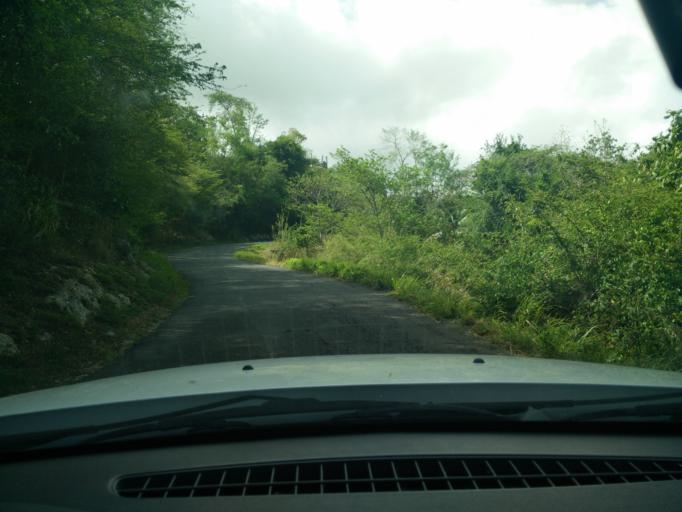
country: GP
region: Guadeloupe
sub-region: Guadeloupe
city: Le Gosier
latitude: 16.2299
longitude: -61.4572
